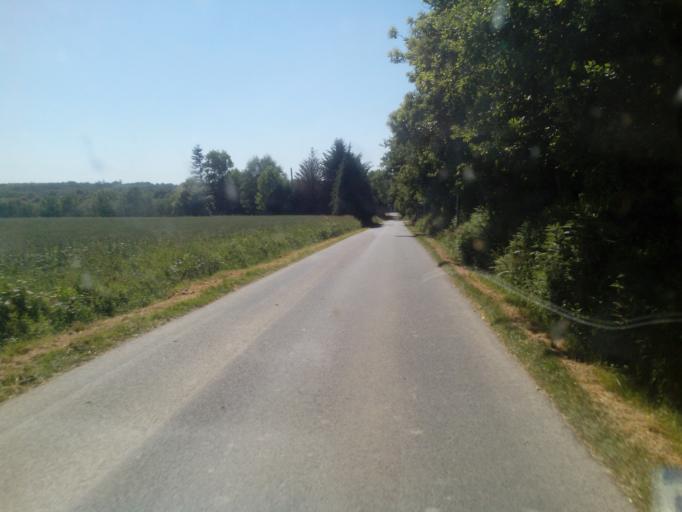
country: FR
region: Brittany
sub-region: Departement des Cotes-d'Armor
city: Merdrignac
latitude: 48.1416
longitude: -2.3695
